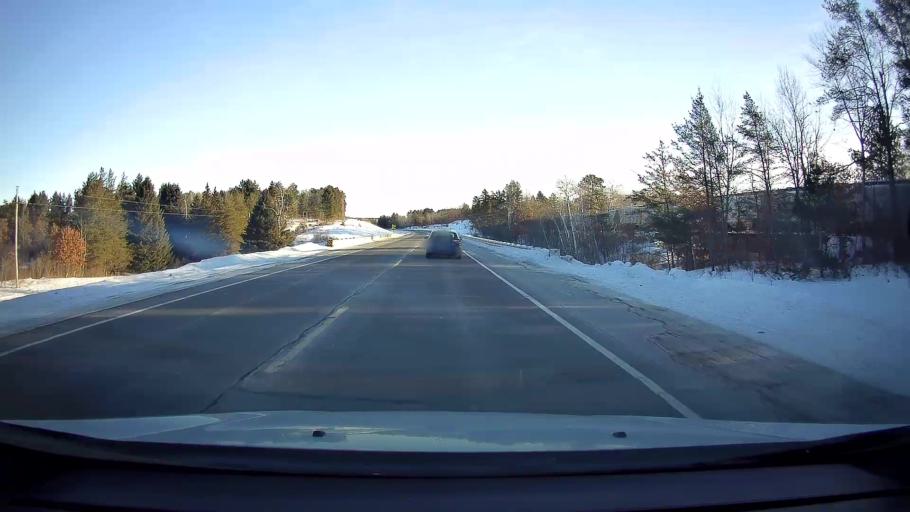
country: US
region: Wisconsin
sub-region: Washburn County
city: Spooner
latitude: 45.9212
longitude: -91.7315
